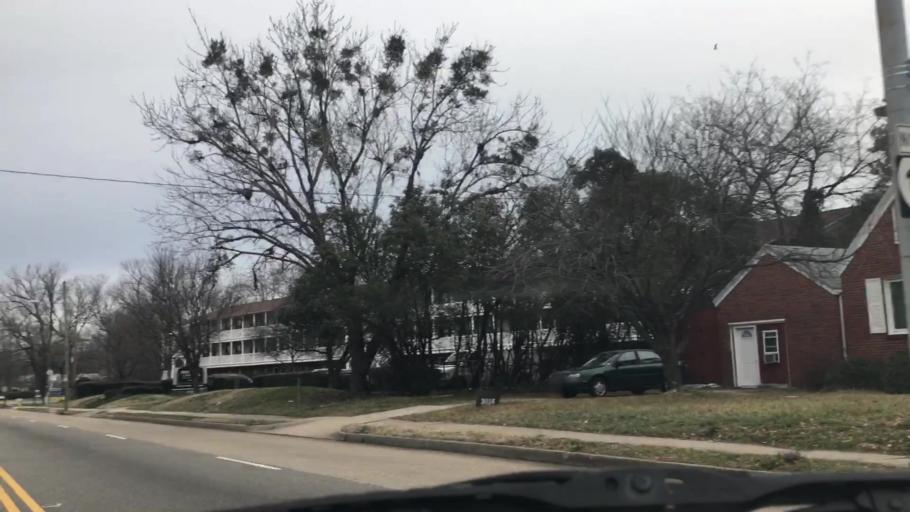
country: US
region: Virginia
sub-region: City of Norfolk
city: Norfolk
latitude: 36.8783
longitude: -76.2333
